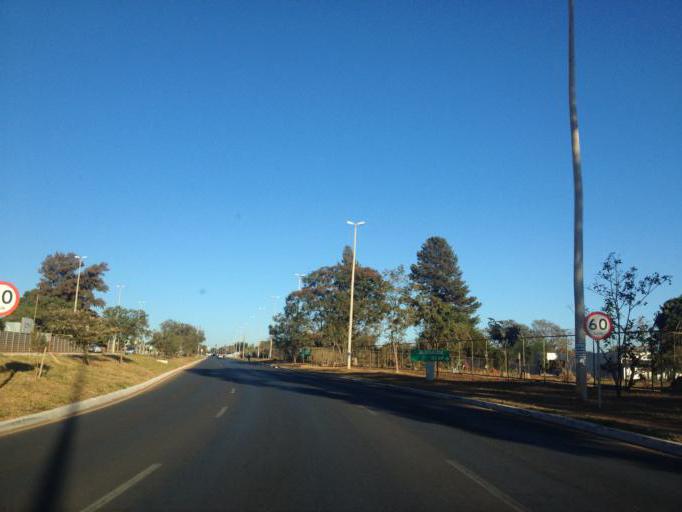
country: BR
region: Federal District
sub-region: Brasilia
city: Brasilia
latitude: -15.7698
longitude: -47.8940
